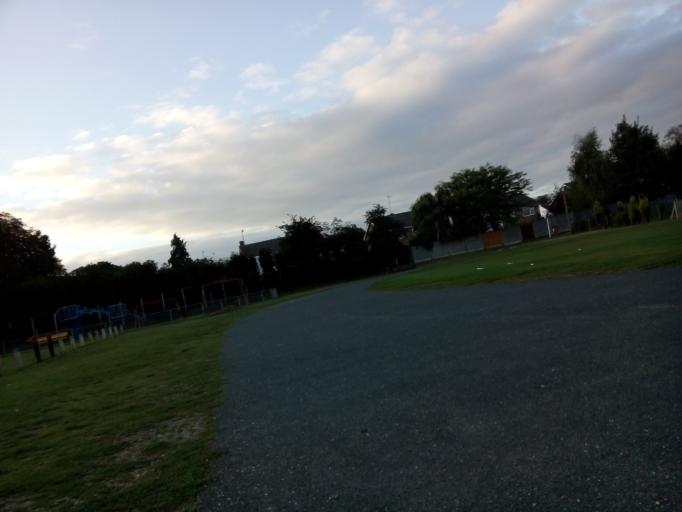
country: GB
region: England
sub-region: Suffolk
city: Bramford
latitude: 52.0601
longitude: 1.0988
